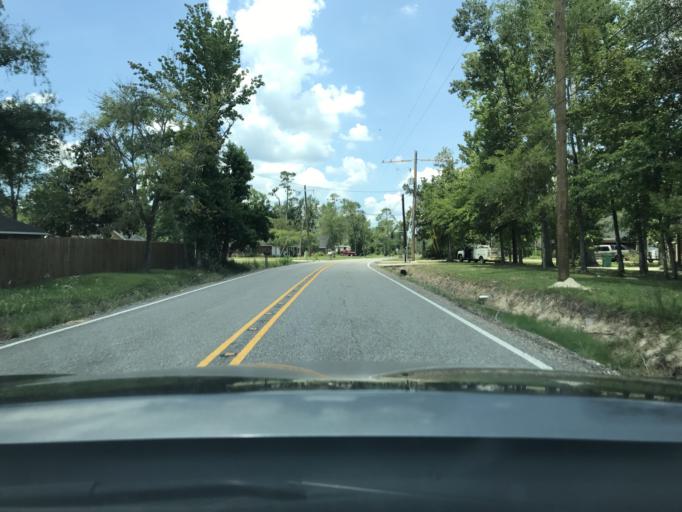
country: US
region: Louisiana
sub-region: Calcasieu Parish
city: Moss Bluff
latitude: 30.3200
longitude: -93.1794
